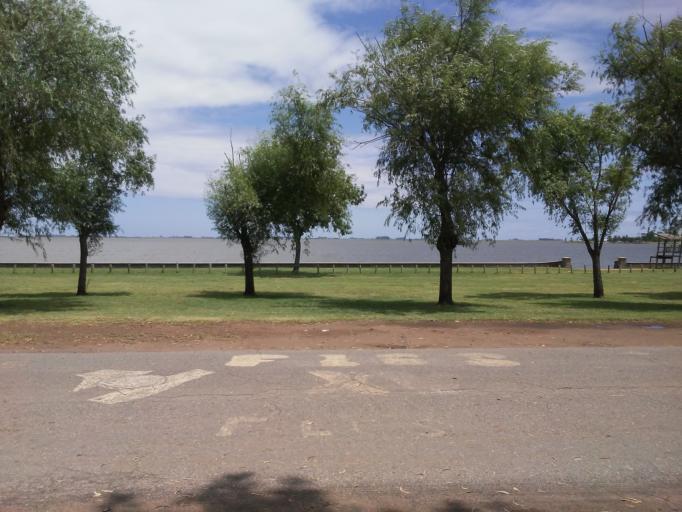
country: AR
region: Buenos Aires
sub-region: Partido de Junin
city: Junin
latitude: -34.6619
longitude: -61.0193
